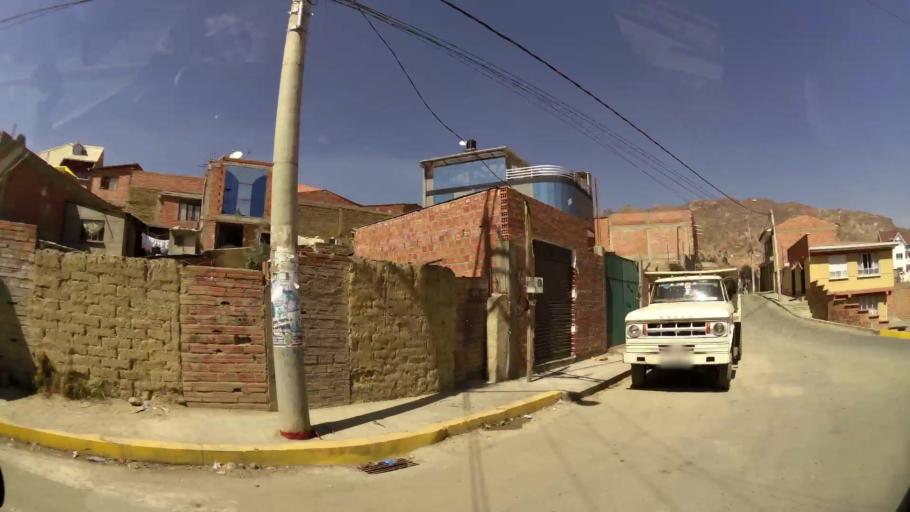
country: BO
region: La Paz
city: La Paz
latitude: -16.5383
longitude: -68.0448
